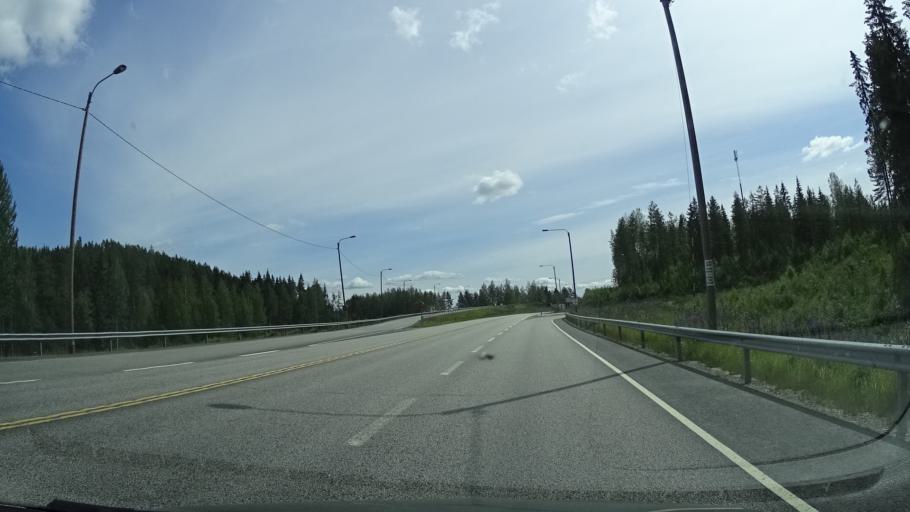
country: FI
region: Central Finland
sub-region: Jyvaeskylae
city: Jyvaeskylae
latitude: 62.2510
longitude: 25.6448
